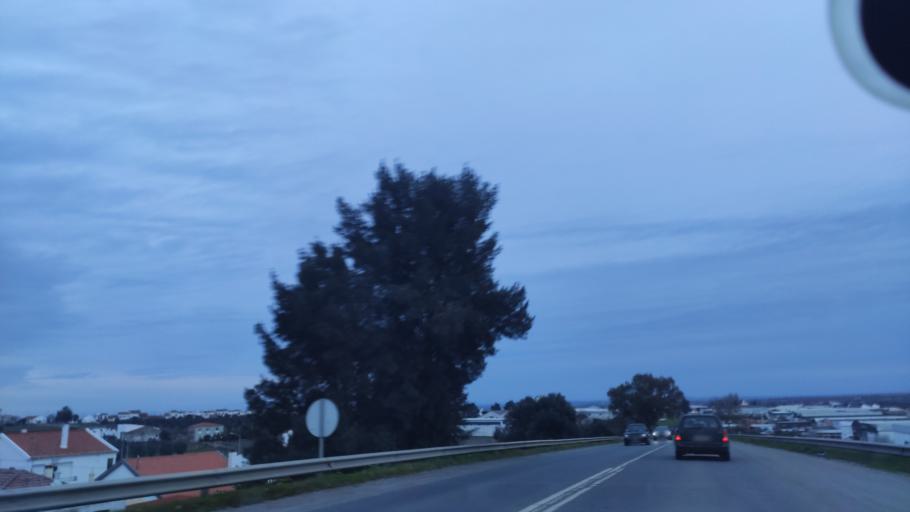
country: PT
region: Beja
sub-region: Beja
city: Beja
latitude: 38.0242
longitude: -7.8581
